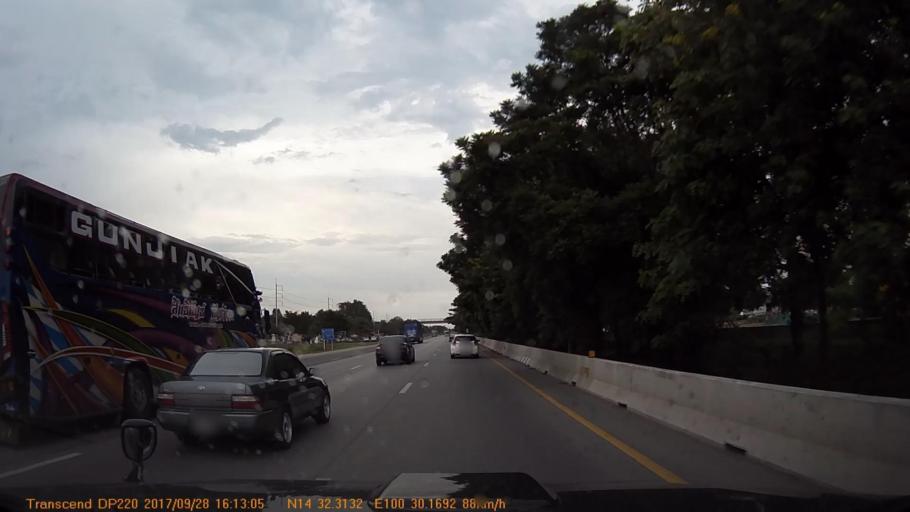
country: TH
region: Phra Nakhon Si Ayutthaya
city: Maha Rat
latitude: 14.5396
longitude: 100.5025
